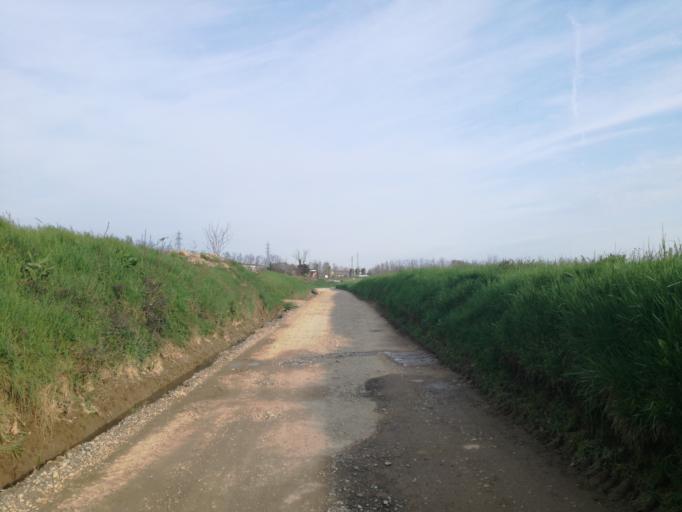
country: IT
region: Lombardy
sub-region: Provincia di Lecco
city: Verderio Superiore
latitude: 45.6688
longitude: 9.4470
